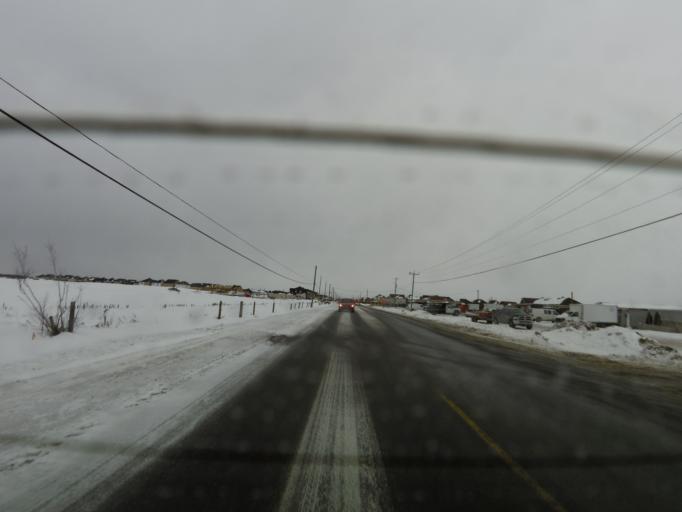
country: CA
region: Ontario
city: Clarence-Rockland
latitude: 45.4406
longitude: -75.4762
